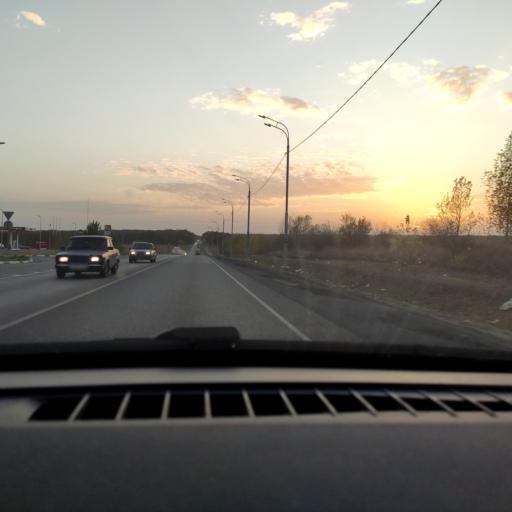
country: RU
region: Voronezj
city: Semiluki
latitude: 51.6459
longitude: 39.0233
